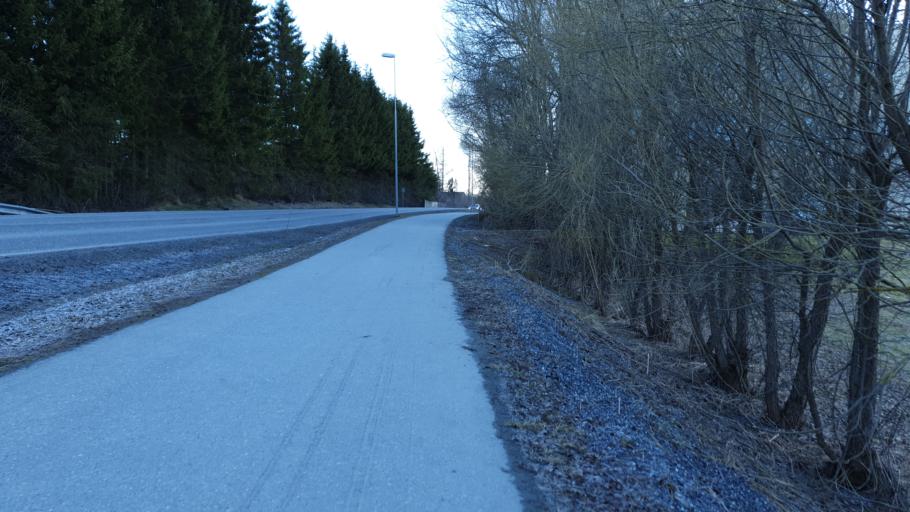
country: NO
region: Sor-Trondelag
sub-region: Orkdal
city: Orkanger
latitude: 63.2916
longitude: 9.8434
